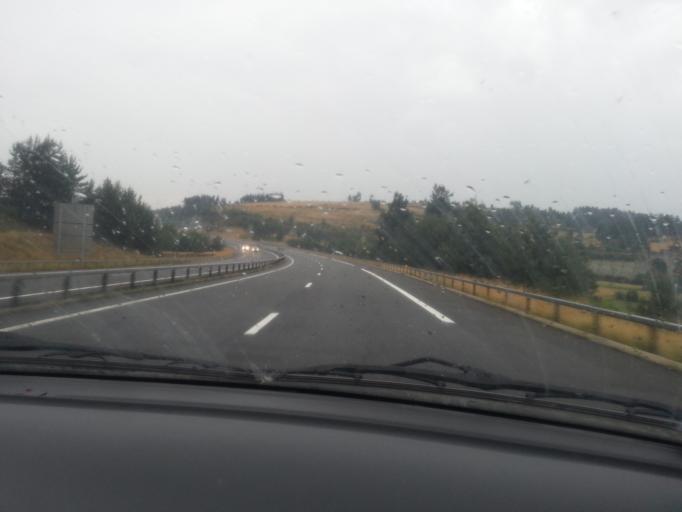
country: FR
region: Languedoc-Roussillon
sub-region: Departement de la Lozere
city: Aumont-Aubrac
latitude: 44.7497
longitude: 3.2895
